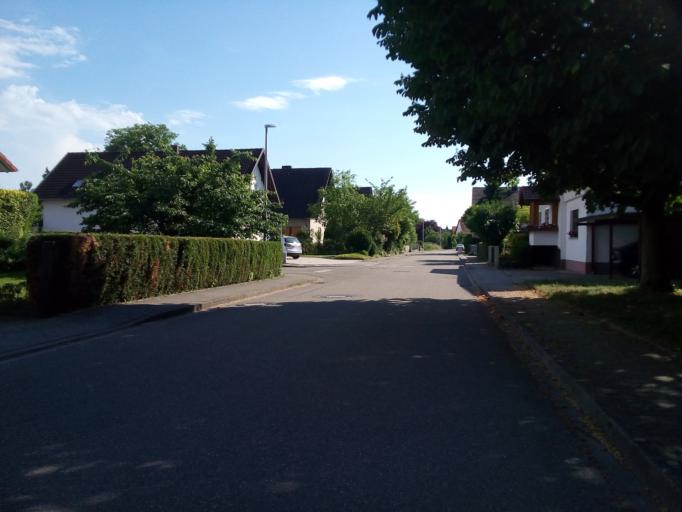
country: DE
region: Baden-Wuerttemberg
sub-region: Karlsruhe Region
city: Lichtenau
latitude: 48.7119
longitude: 8.0009
